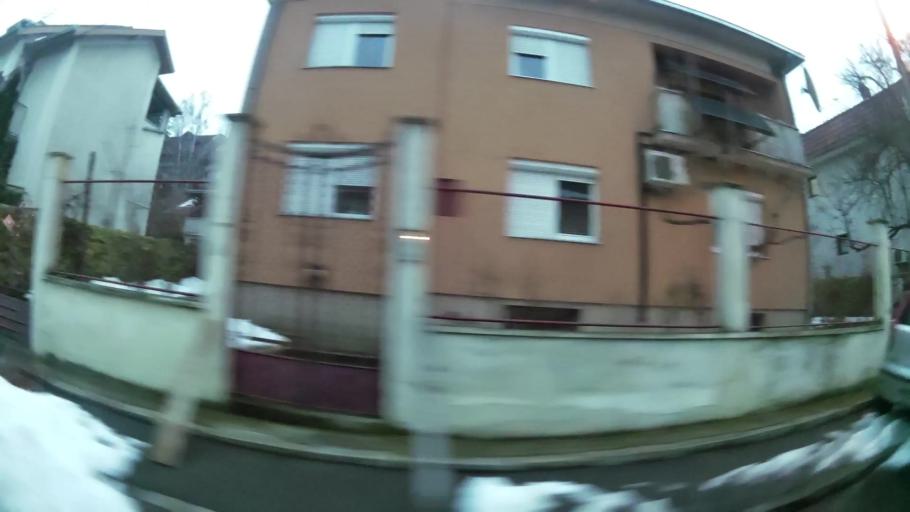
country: RS
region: Central Serbia
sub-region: Belgrade
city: Vozdovac
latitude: 44.7749
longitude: 20.4873
